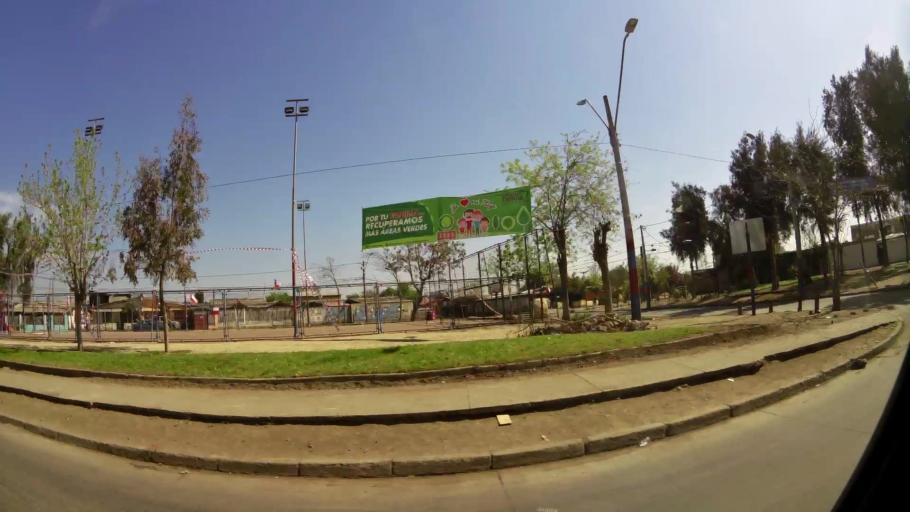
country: CL
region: Santiago Metropolitan
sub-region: Provincia de Santiago
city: Lo Prado
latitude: -33.4751
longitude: -70.7089
